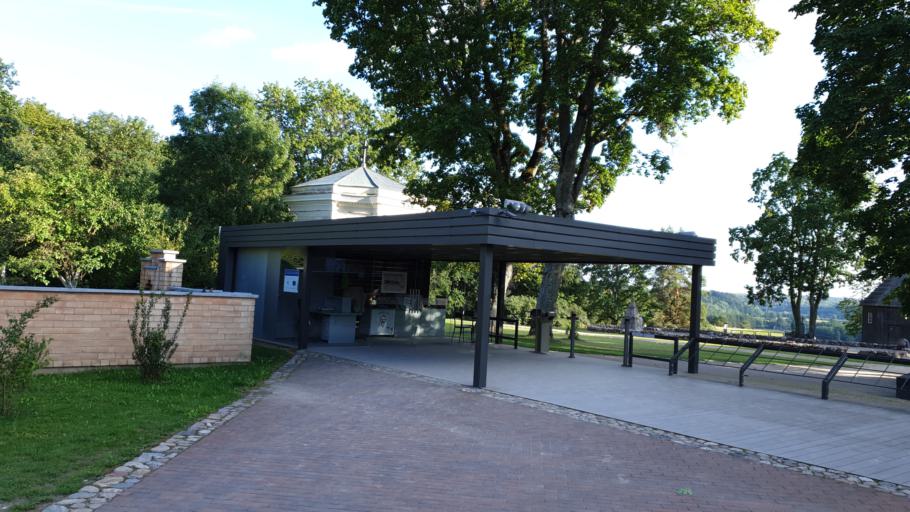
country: LT
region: Vilnius County
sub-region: Vilniaus Rajonas
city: Vievis
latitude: 54.8851
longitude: 24.8525
